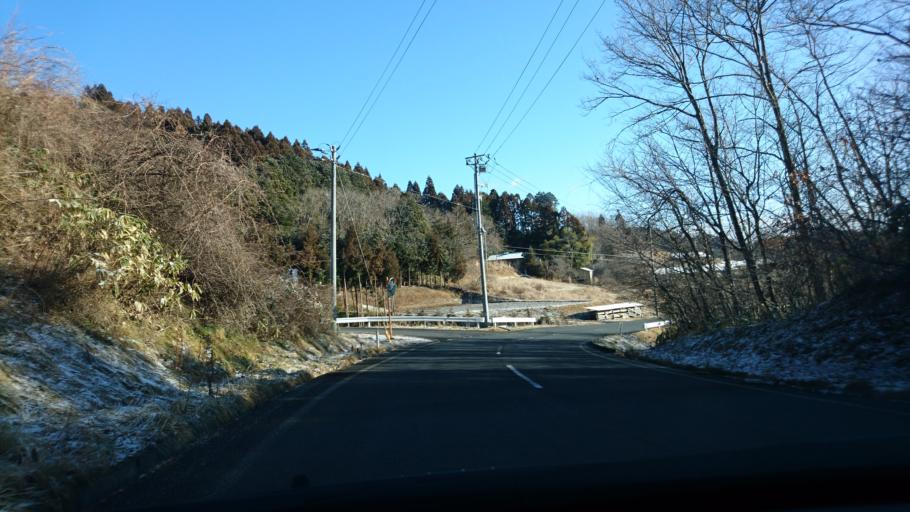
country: JP
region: Iwate
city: Ichinoseki
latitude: 38.8778
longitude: 141.3112
